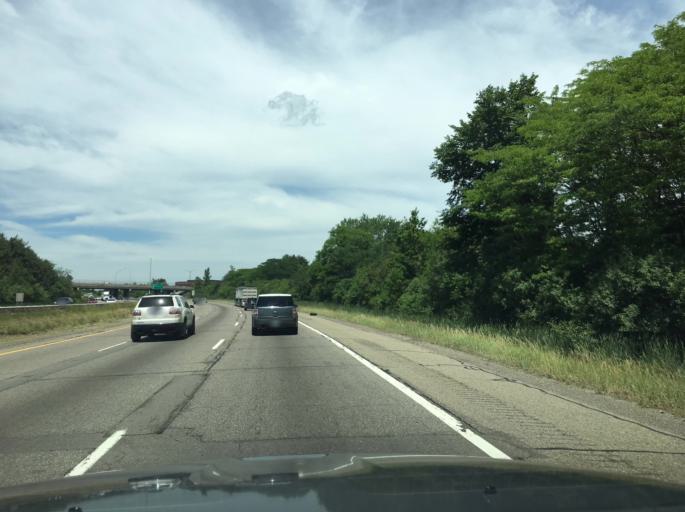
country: US
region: Michigan
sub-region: Oakland County
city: Troy
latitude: 42.6030
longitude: -83.1654
